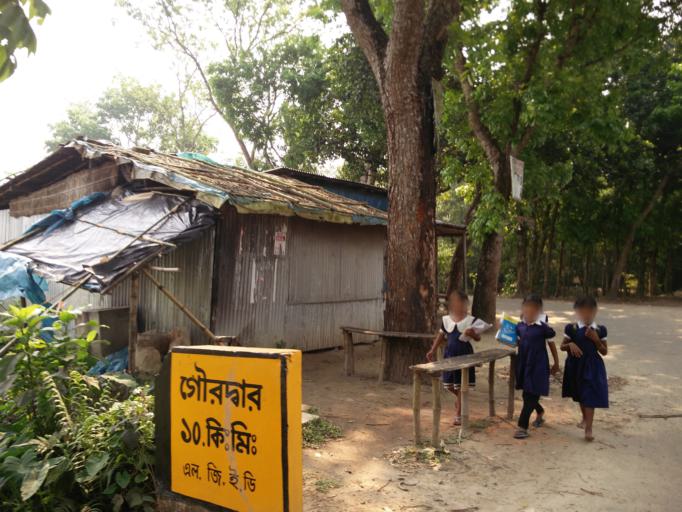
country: BD
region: Dhaka
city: Muktagacha
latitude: 24.9047
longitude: 90.1872
